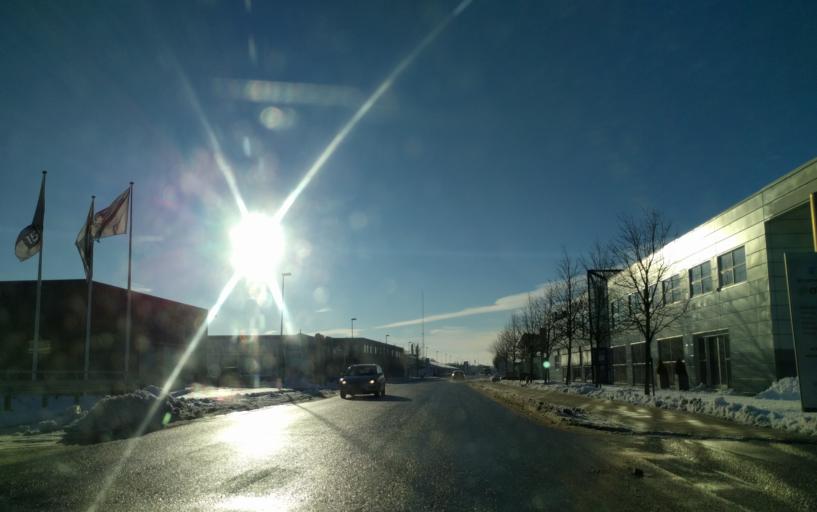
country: DK
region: North Denmark
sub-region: Alborg Kommune
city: Aalborg
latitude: 57.0364
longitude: 9.9270
